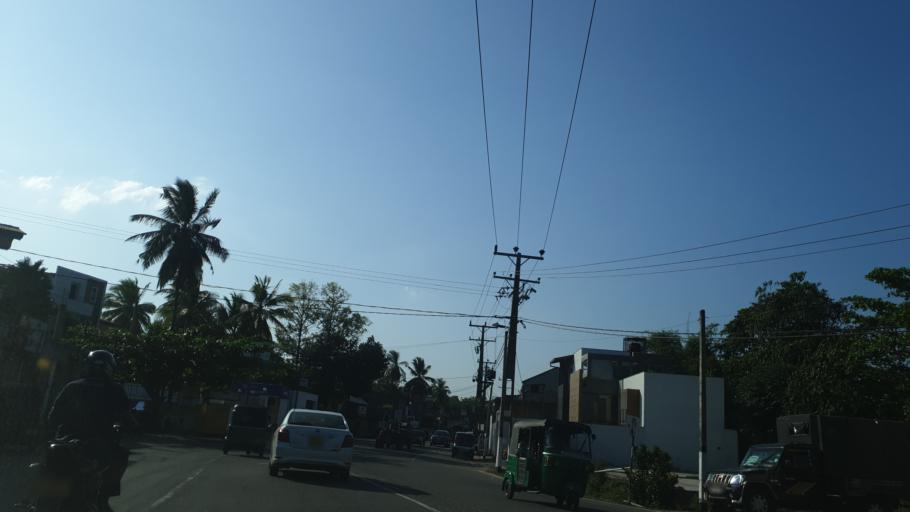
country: LK
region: Western
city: Sri Jayewardenepura Kotte
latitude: 6.8769
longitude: 79.9265
